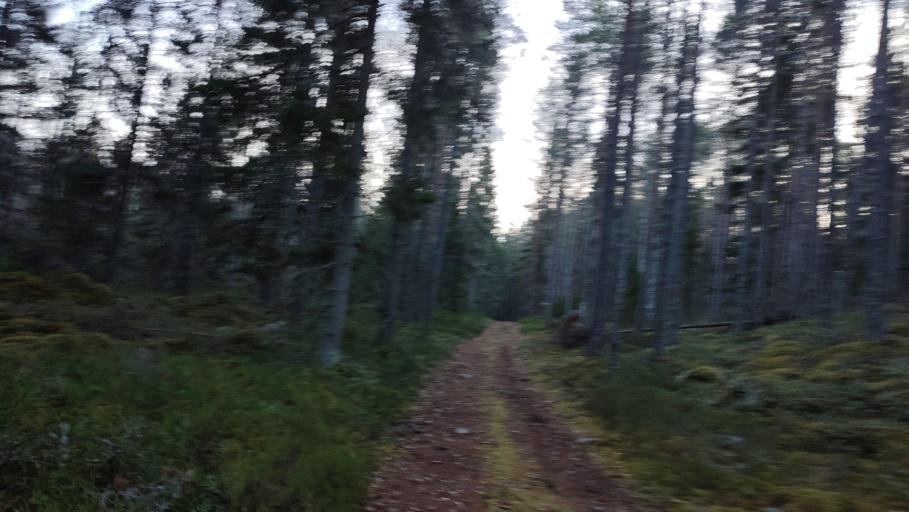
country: FI
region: Southern Ostrobothnia
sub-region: Suupohja
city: Karijoki
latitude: 62.2747
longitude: 21.6325
